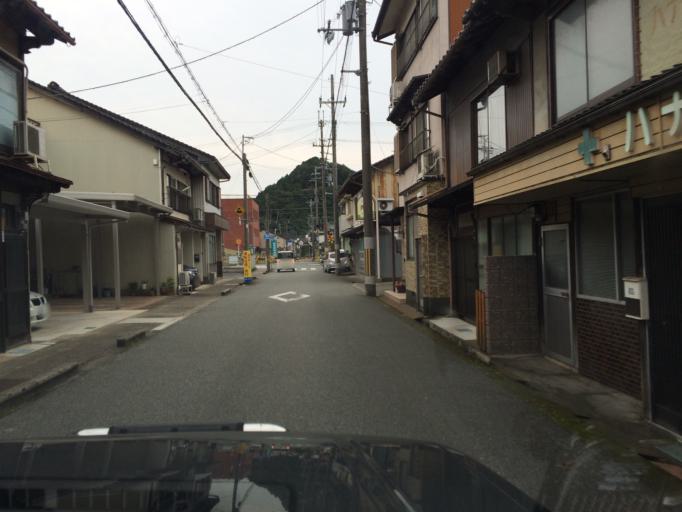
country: JP
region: Hyogo
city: Toyooka
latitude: 35.4672
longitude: 134.7731
